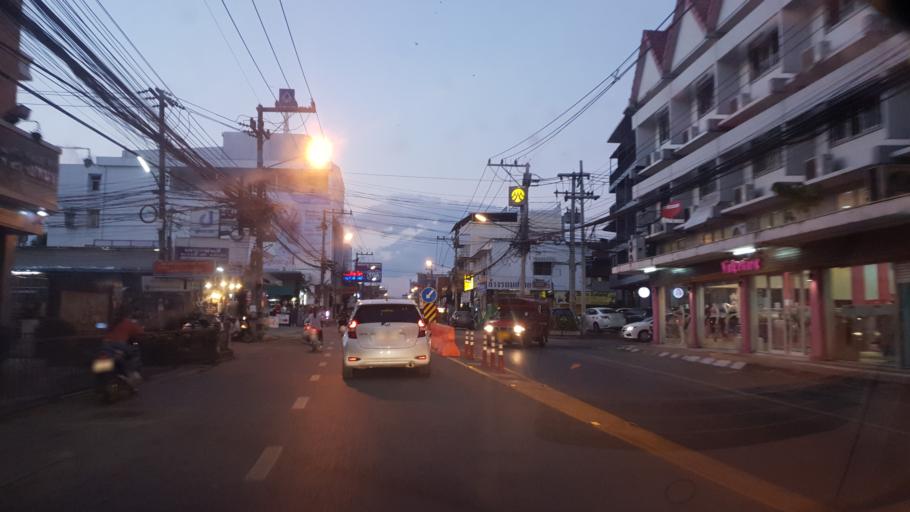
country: TH
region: Chiang Mai
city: Chiang Mai
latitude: 18.7982
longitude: 98.9862
